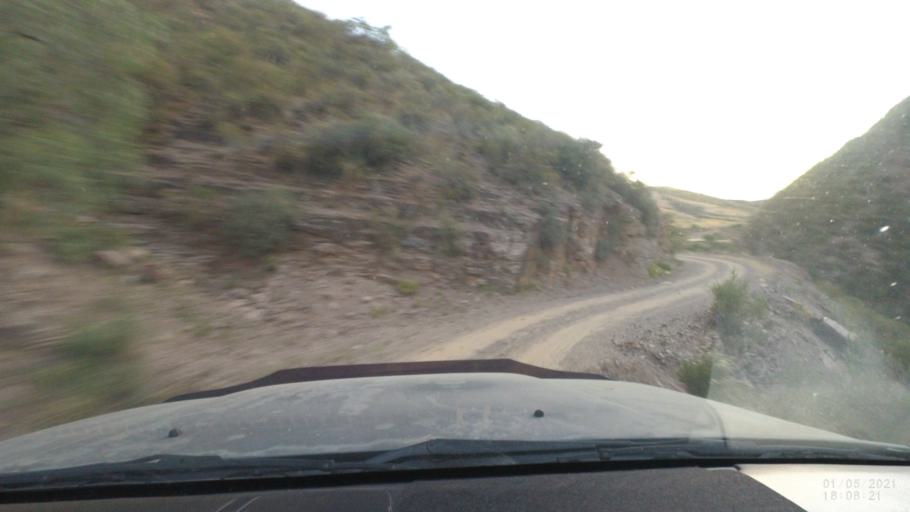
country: BO
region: Cochabamba
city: Capinota
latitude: -17.6851
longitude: -66.1902
